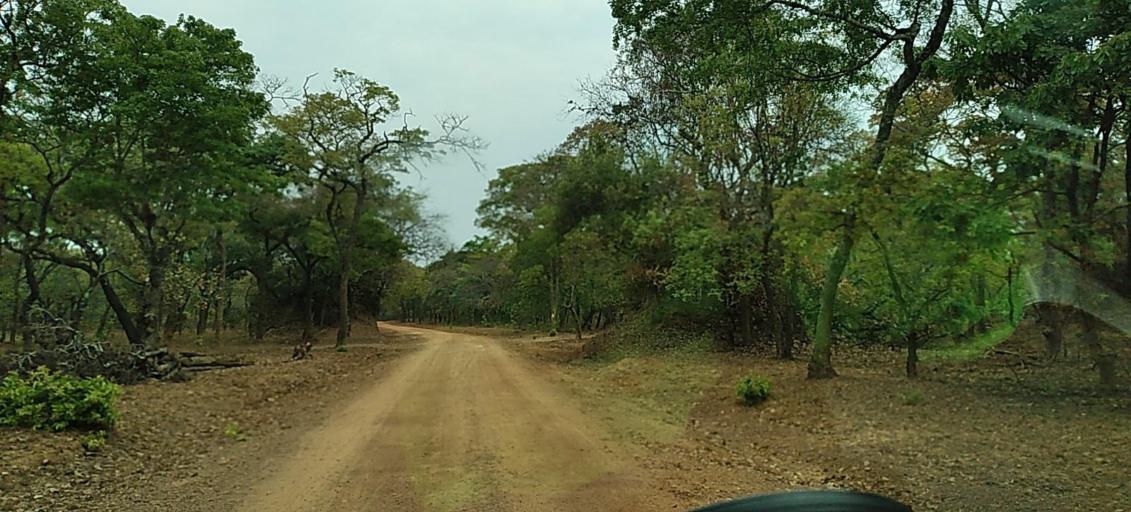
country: ZM
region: North-Western
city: Solwezi
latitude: -12.9200
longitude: 26.5601
